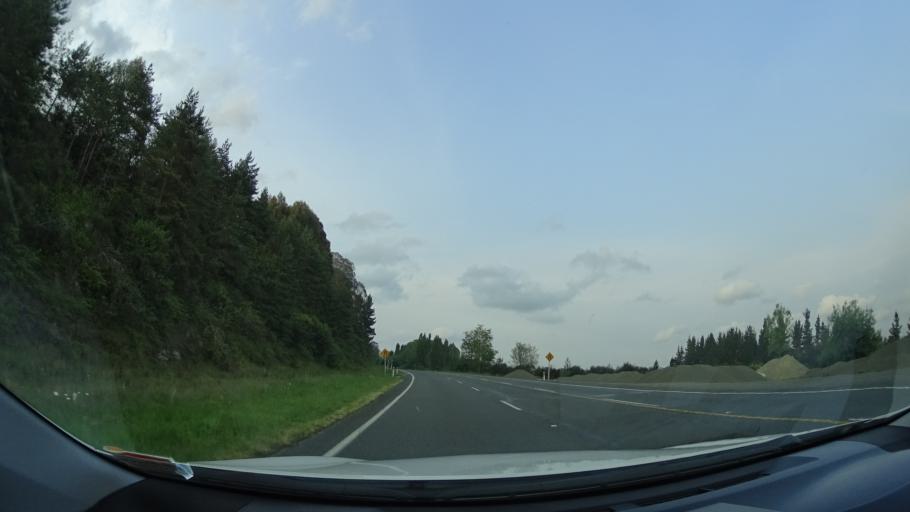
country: NZ
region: Manawatu-Wanganui
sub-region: Ruapehu District
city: Waiouru
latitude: -39.7495
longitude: 175.8350
